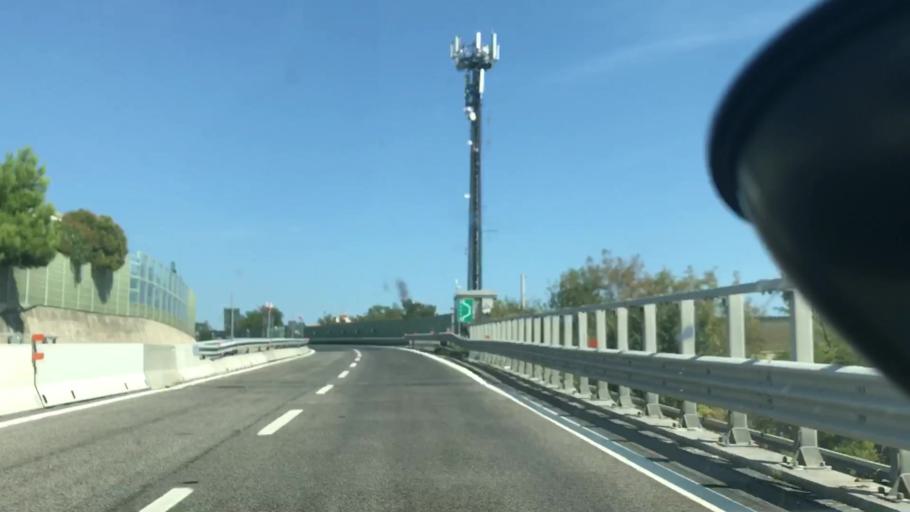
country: IT
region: Abruzzo
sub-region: Provincia di Chieti
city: Vasto
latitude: 42.0951
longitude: 14.6981
